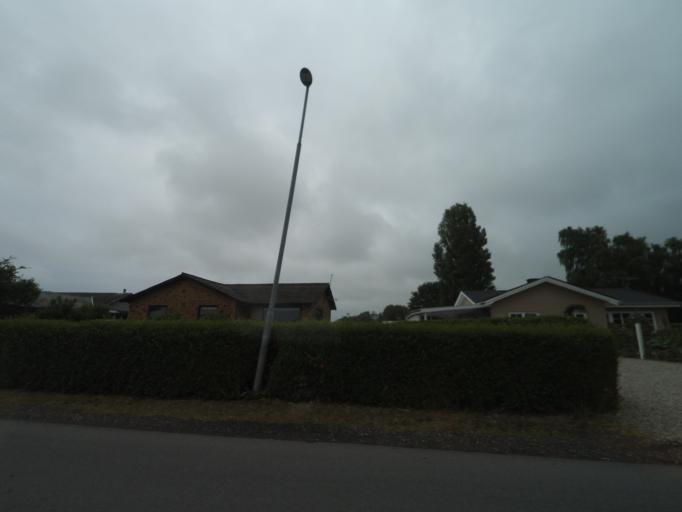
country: DK
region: South Denmark
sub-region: Nordfyns Kommune
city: Otterup
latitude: 55.5725
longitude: 10.3924
